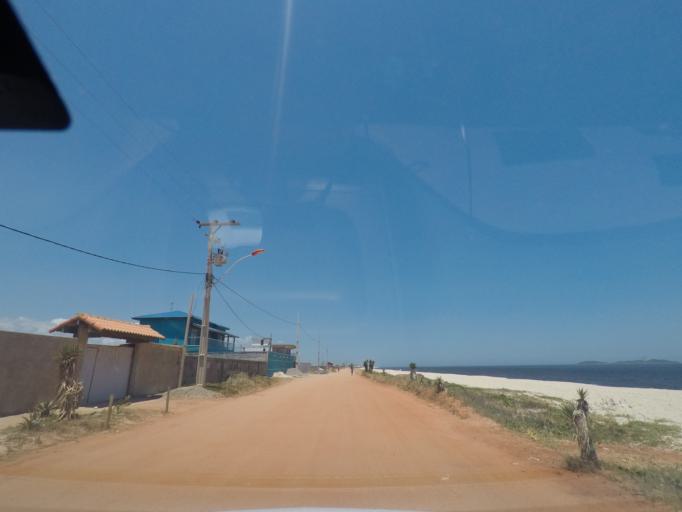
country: BR
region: Rio de Janeiro
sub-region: Niteroi
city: Niteroi
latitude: -22.9692
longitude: -42.9745
